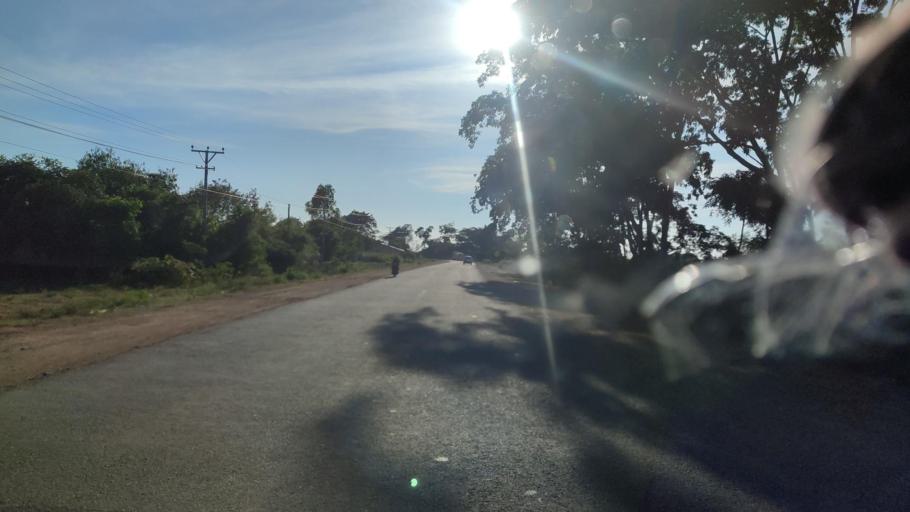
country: MM
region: Mandalay
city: Yamethin
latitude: 20.7368
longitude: 96.2086
